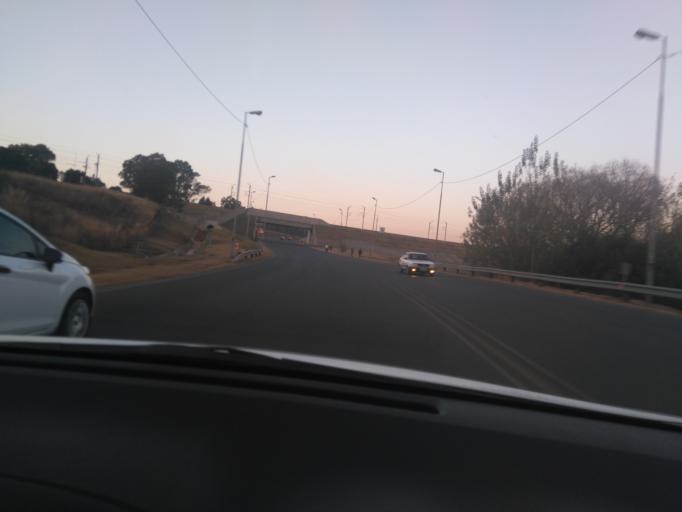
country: ZA
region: Gauteng
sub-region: City of Johannesburg Metropolitan Municipality
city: Modderfontein
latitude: -26.1022
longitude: 28.1701
